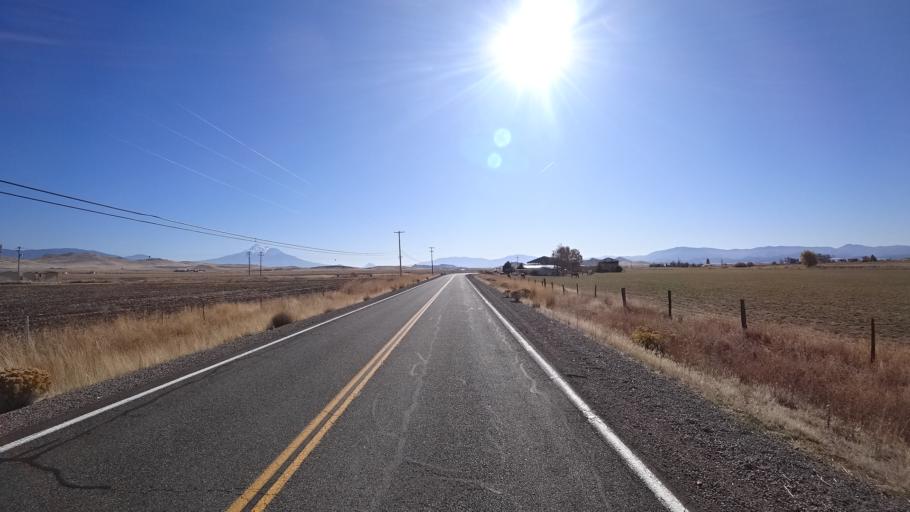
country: US
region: California
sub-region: Siskiyou County
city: Montague
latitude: 41.7790
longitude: -122.4737
